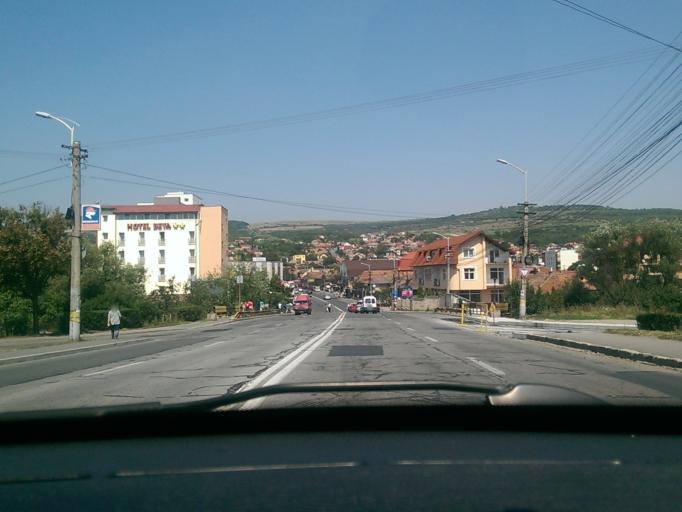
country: RO
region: Cluj
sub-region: Municipiul Cluj-Napoca
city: Cluj-Napoca
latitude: 46.7851
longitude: 23.5819
